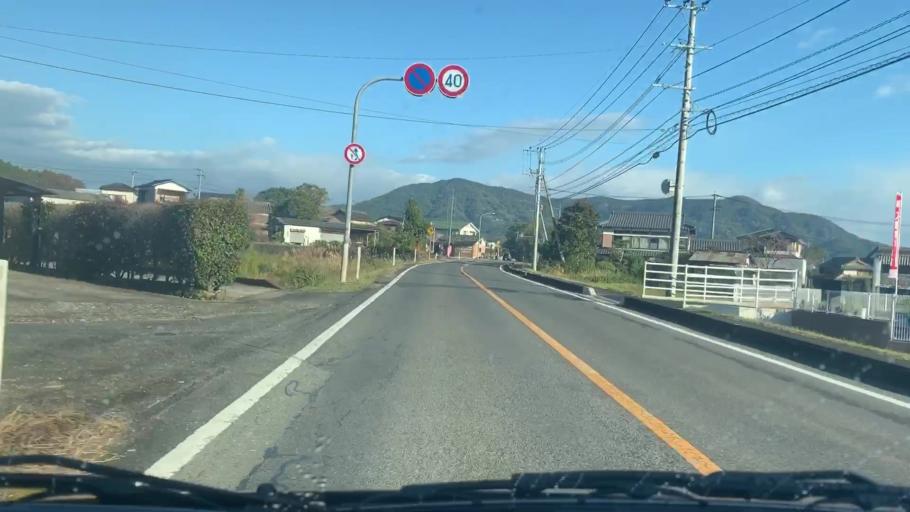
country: JP
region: Saga Prefecture
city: Takeocho-takeo
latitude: 33.2142
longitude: 130.0286
